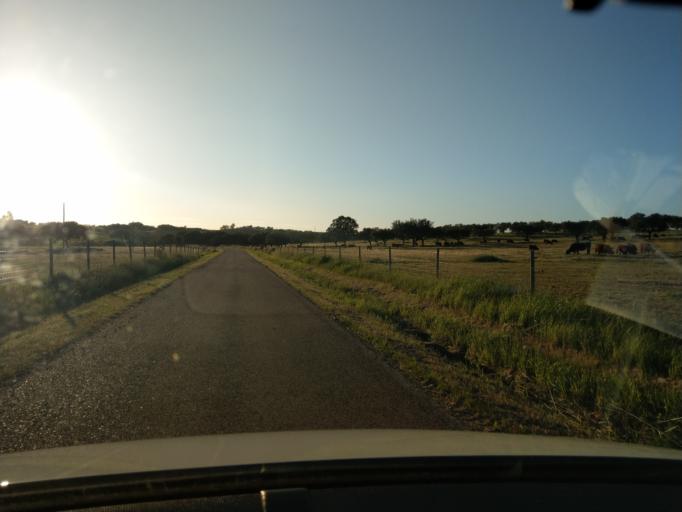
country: PT
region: Portalegre
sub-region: Campo Maior
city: Campo Maior
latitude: 39.1017
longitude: -7.0602
